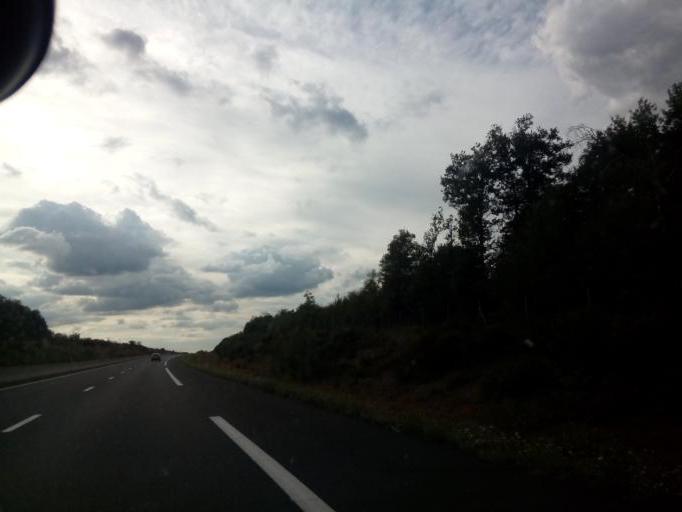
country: FR
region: Centre
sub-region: Departement du Loir-et-Cher
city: Faverolles-sur-Cher
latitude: 47.2960
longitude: 1.2398
